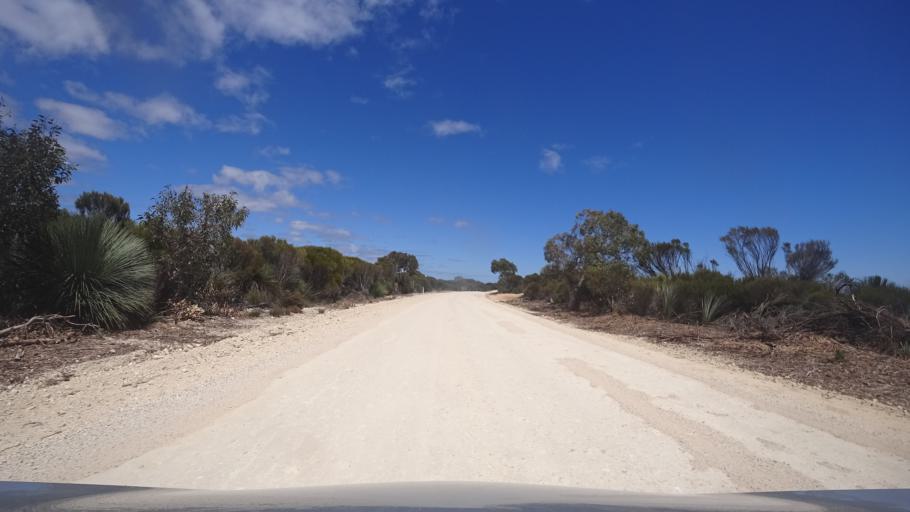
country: AU
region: South Australia
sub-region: Kangaroo Island
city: Kingscote
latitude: -35.6394
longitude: 137.2335
